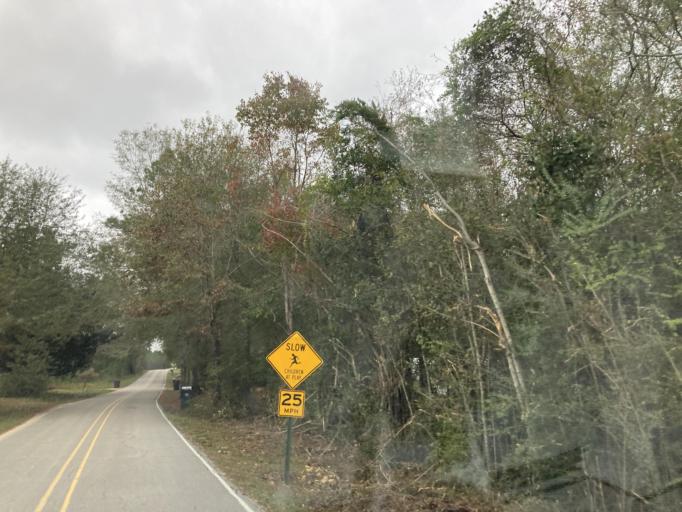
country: US
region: Mississippi
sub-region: Lamar County
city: Purvis
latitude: 31.1782
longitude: -89.4192
